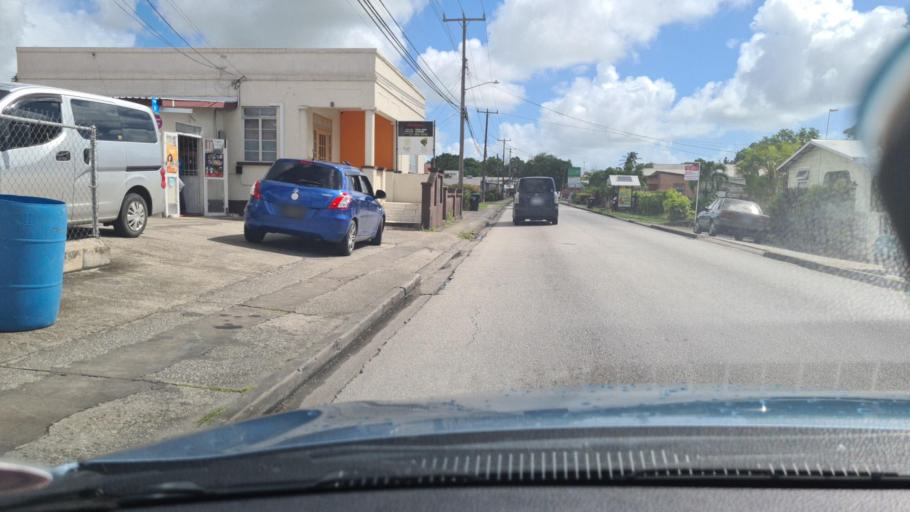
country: BB
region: Saint Michael
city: Bridgetown
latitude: 13.0867
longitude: -59.5742
